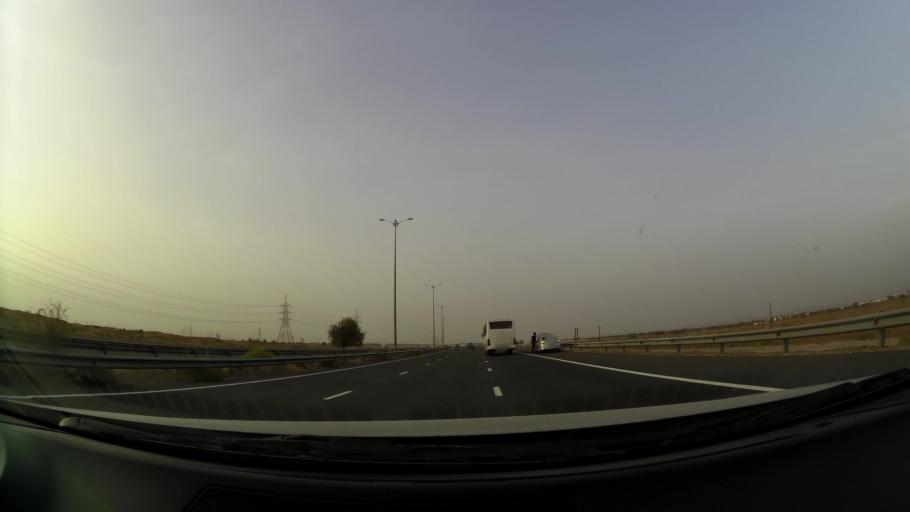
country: OM
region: Al Buraimi
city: Al Buraymi
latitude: 24.3690
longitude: 55.7940
